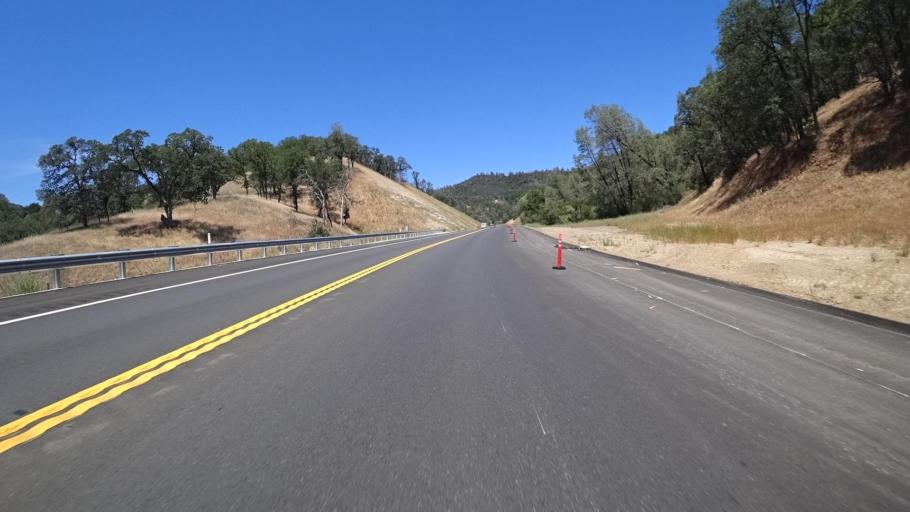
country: US
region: California
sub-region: Lake County
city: Hidden Valley Lake
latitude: 38.8335
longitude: -122.5890
